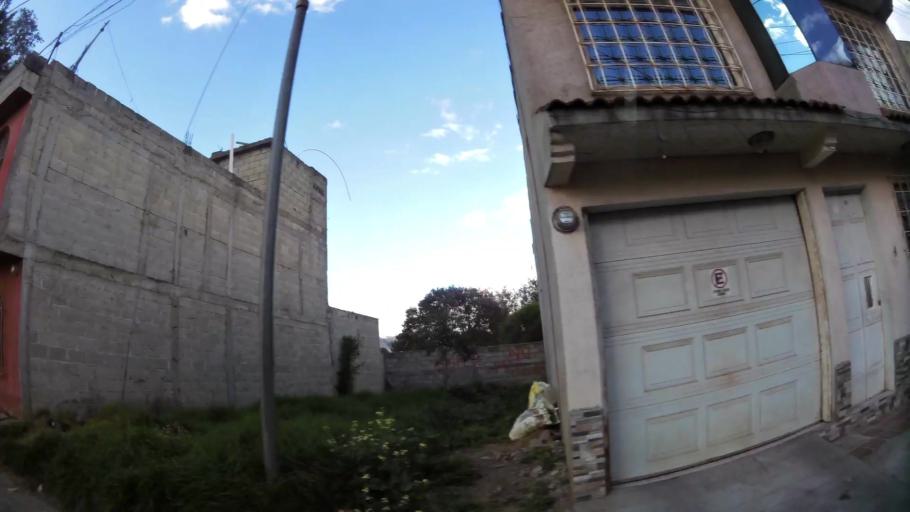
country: GT
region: Quetzaltenango
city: Quetzaltenango
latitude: 14.8533
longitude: -91.5307
